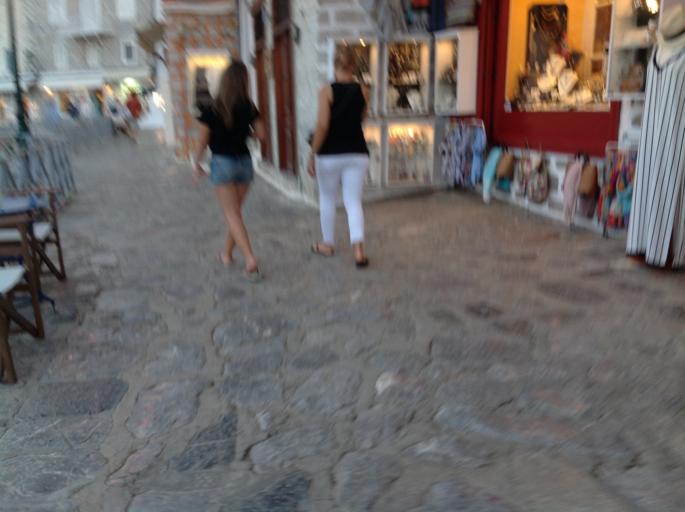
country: GR
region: Attica
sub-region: Nomos Piraios
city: Ydra
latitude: 37.3506
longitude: 23.4647
